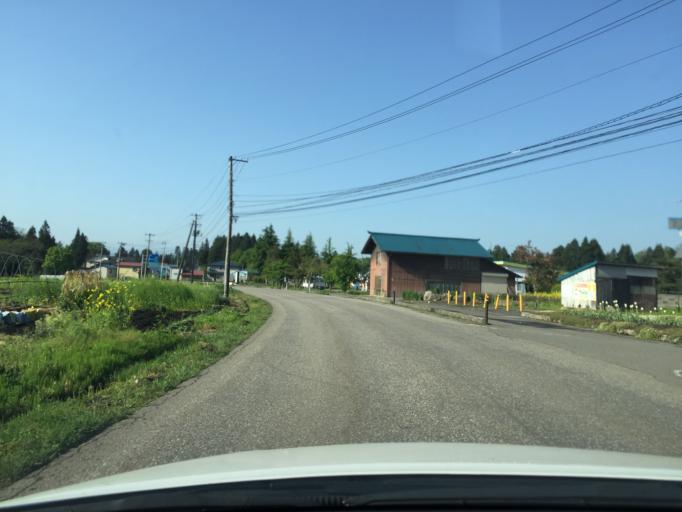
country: JP
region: Fukushima
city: Kitakata
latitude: 37.6506
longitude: 139.7743
